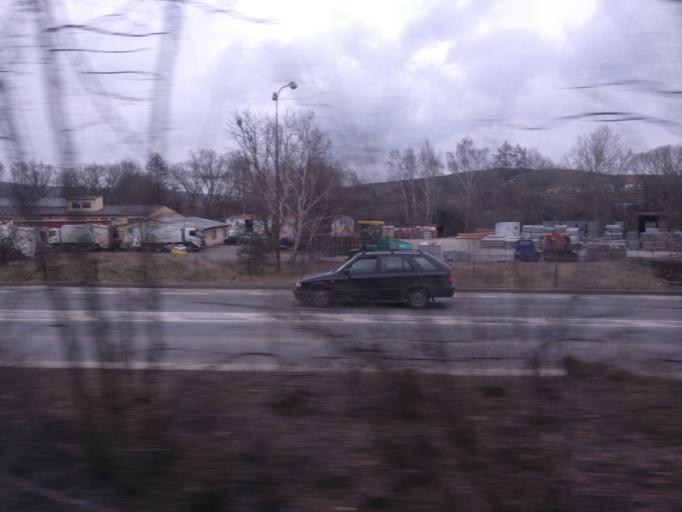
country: CZ
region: South Moravian
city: Zastavka
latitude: 49.1834
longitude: 16.3729
